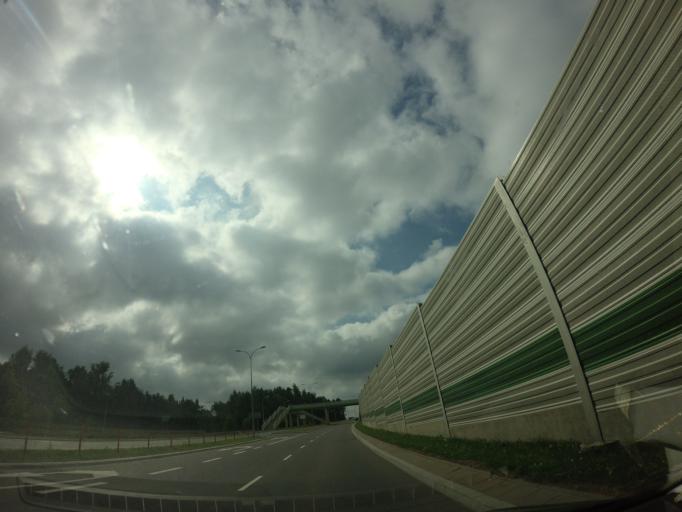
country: PL
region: Podlasie
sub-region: Bialystok
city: Bialystok
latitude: 53.1345
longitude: 23.2216
